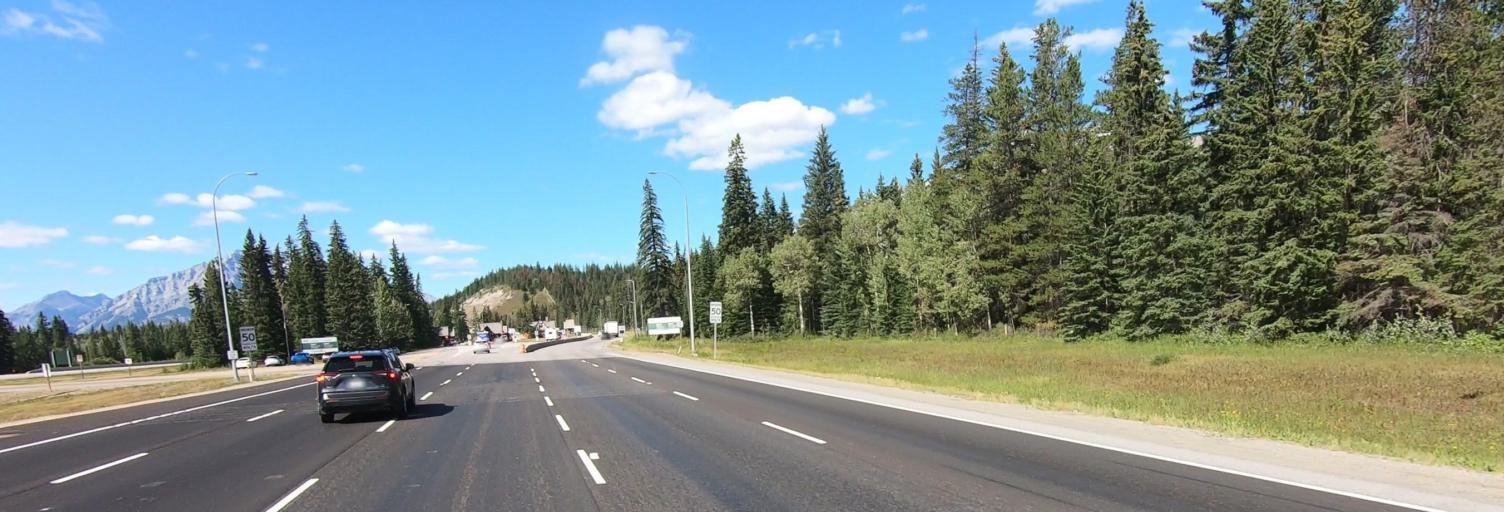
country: CA
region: Alberta
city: Canmore
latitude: 51.1336
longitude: -115.4042
